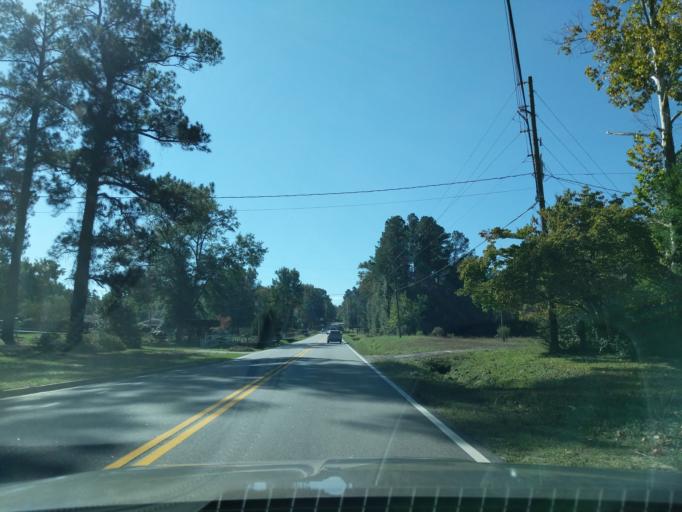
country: US
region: Georgia
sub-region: Richmond County
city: Hephzibah
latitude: 33.3370
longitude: -82.0071
